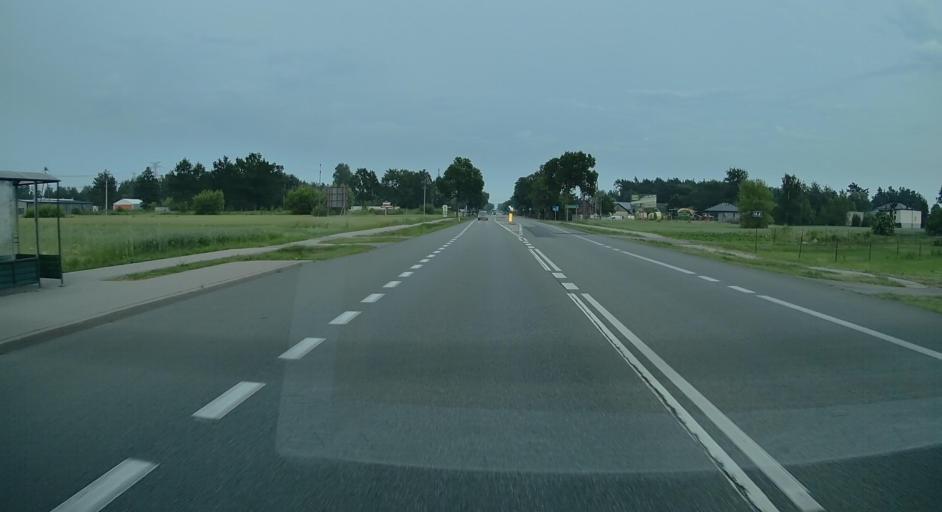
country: PL
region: Masovian Voivodeship
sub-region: Siedlce
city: Siedlce
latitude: 52.1252
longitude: 22.3458
